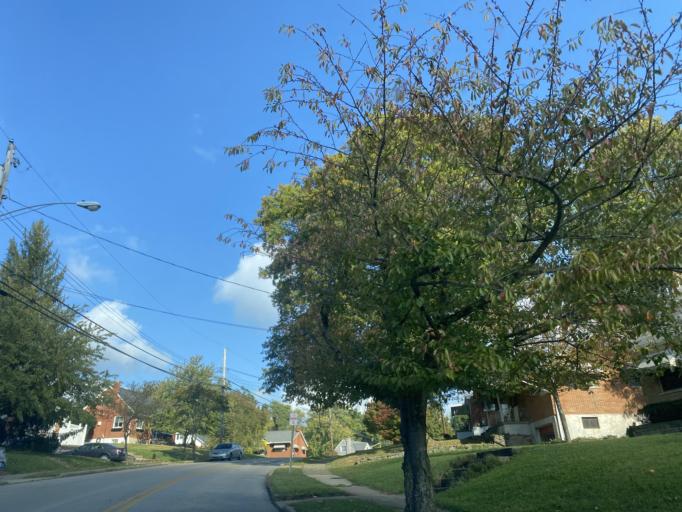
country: US
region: Kentucky
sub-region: Campbell County
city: Fort Thomas
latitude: 39.0923
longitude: -84.4573
